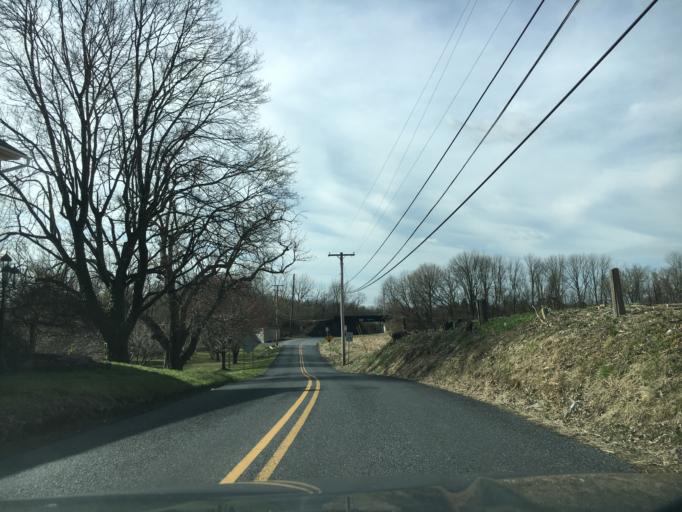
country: US
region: Pennsylvania
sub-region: Northampton County
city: North Catasauqua
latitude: 40.6876
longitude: -75.4527
